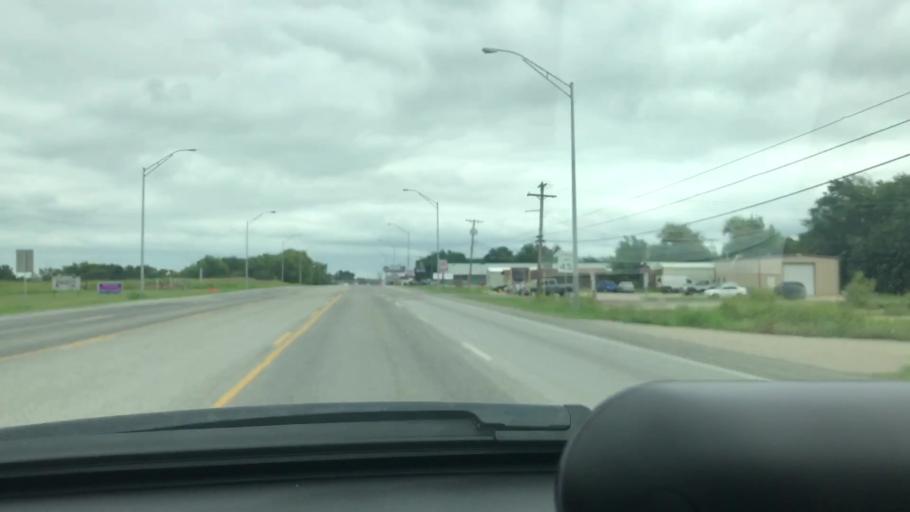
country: US
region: Oklahoma
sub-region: Wagoner County
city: Wagoner
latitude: 35.9506
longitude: -95.3952
